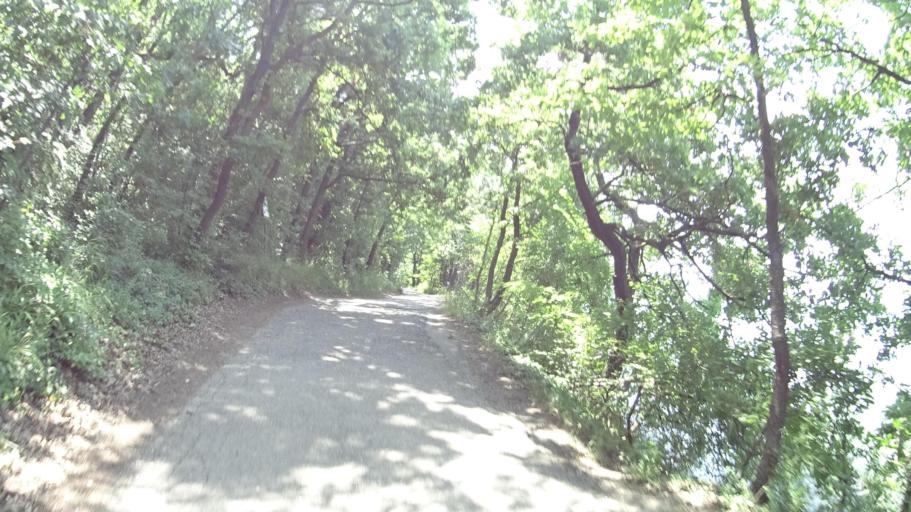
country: HU
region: Veszprem
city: Tihany
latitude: 46.9064
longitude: 17.8499
